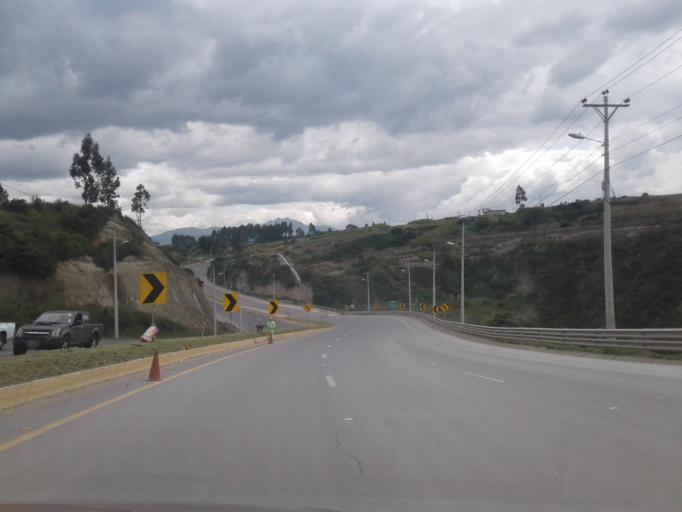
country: EC
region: Pichincha
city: Sangolqui
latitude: -0.3019
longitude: -78.3605
